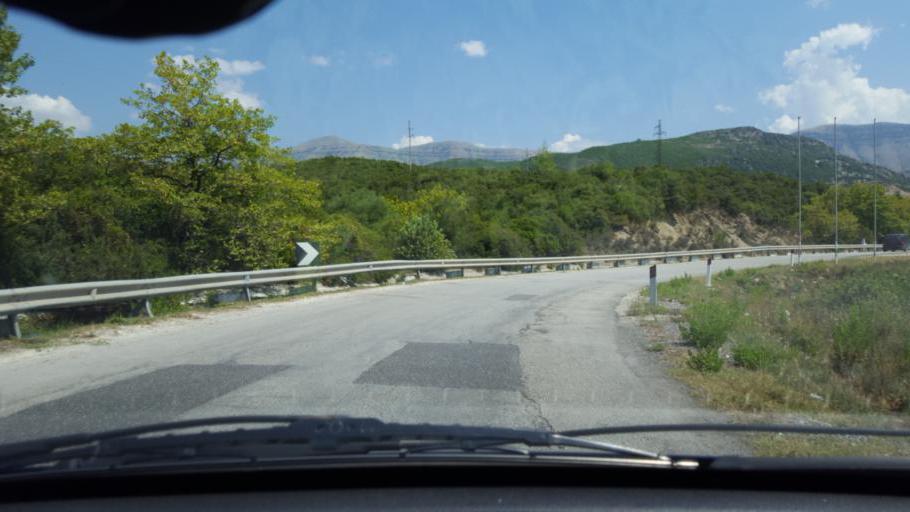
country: AL
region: Vlore
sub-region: Rrethi i Delvines
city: Mesopotam
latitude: 39.9117
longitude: 20.1281
